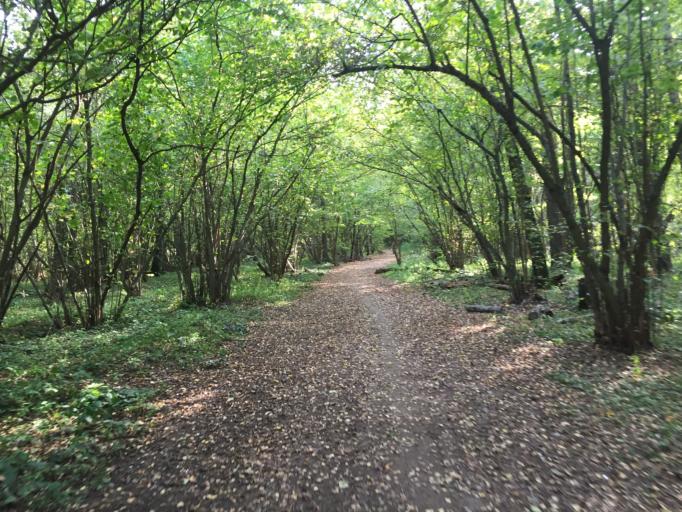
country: RU
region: Moscow
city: Babushkin
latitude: 55.8683
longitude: 37.7298
